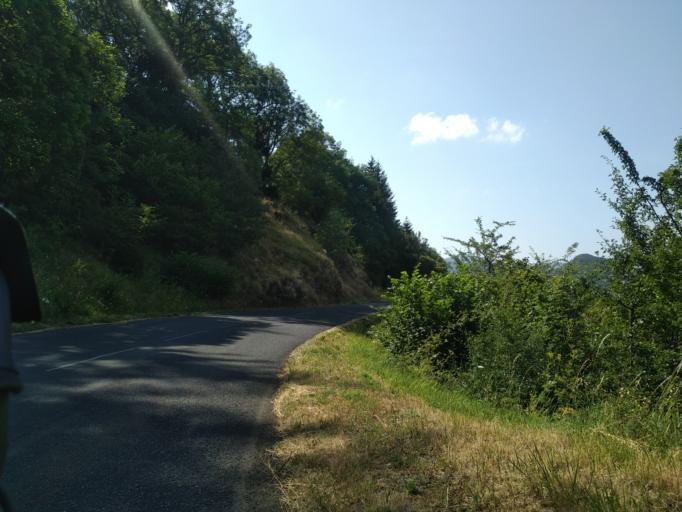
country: FR
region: Auvergne
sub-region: Departement du Cantal
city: Riom-es-Montagnes
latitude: 45.2019
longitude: 2.7168
